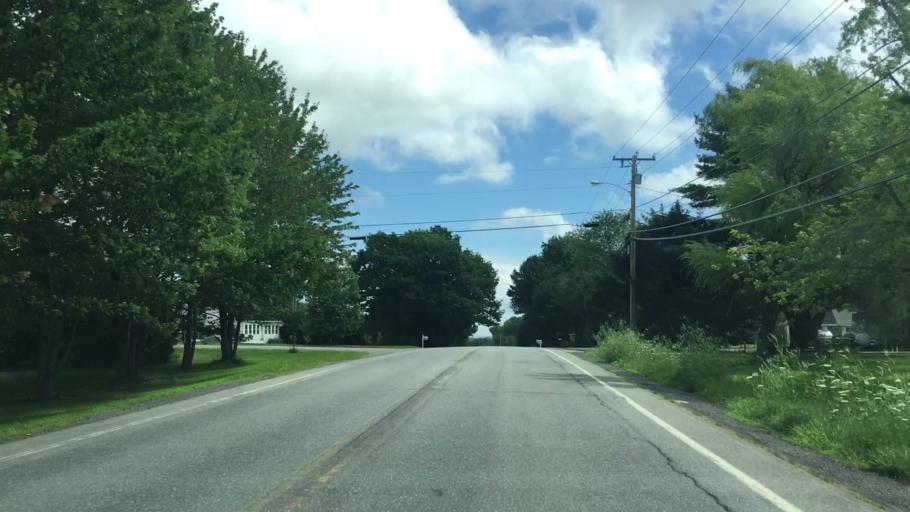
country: US
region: Maine
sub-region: Penobscot County
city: Hermon
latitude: 44.8070
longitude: -68.9374
